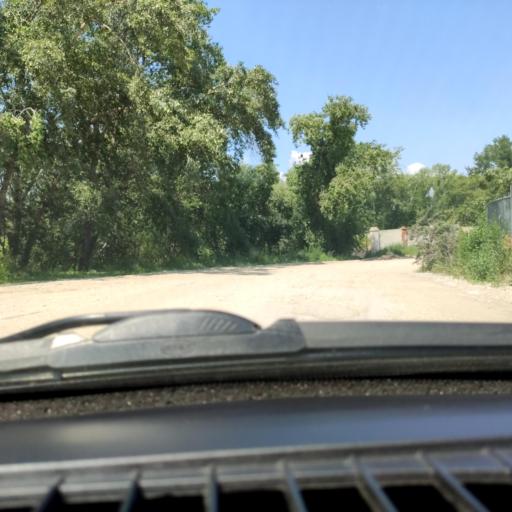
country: RU
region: Samara
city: Zhigulevsk
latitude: 53.4501
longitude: 49.5348
